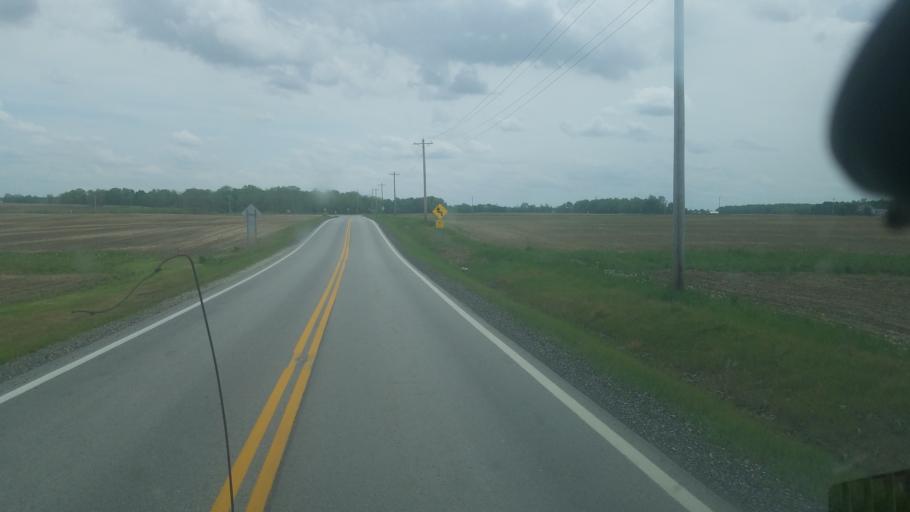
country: US
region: Ohio
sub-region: Crawford County
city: Bucyrus
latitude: 40.9527
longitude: -83.0692
